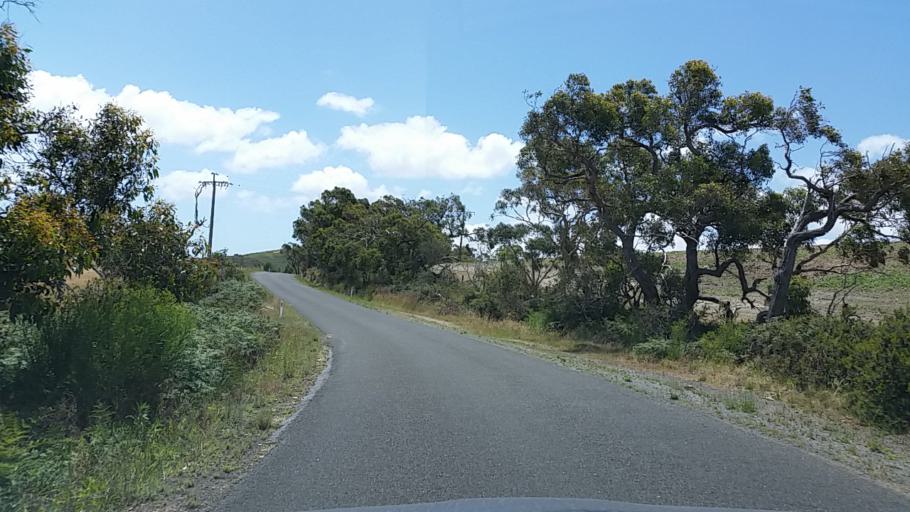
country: AU
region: South Australia
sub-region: Victor Harbor
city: Victor Harbor
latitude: -35.4505
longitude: 138.5929
